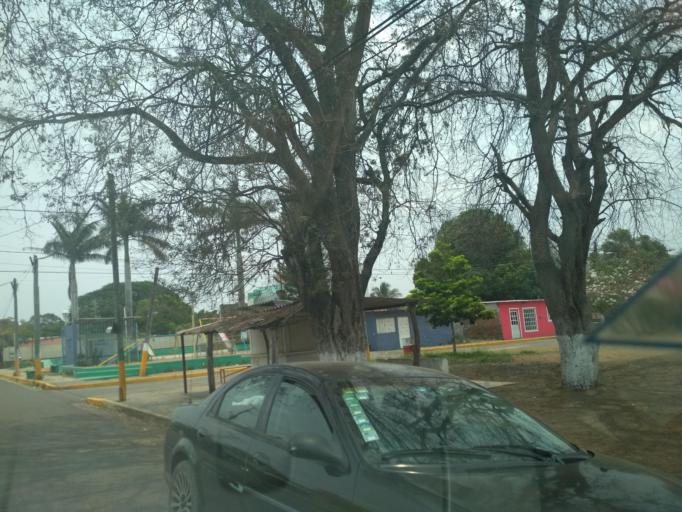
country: MX
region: Veracruz
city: Manlio Fabio Altamirano
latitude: 19.1314
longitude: -96.2966
